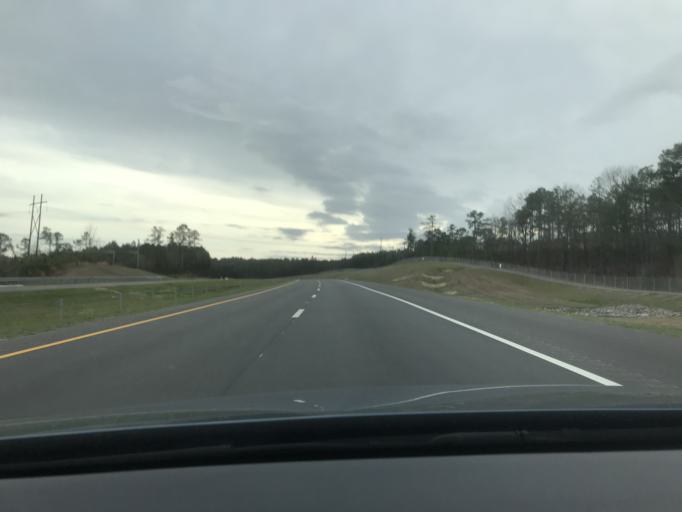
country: US
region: North Carolina
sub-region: Cumberland County
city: Fort Bragg
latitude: 35.0961
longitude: -79.0258
